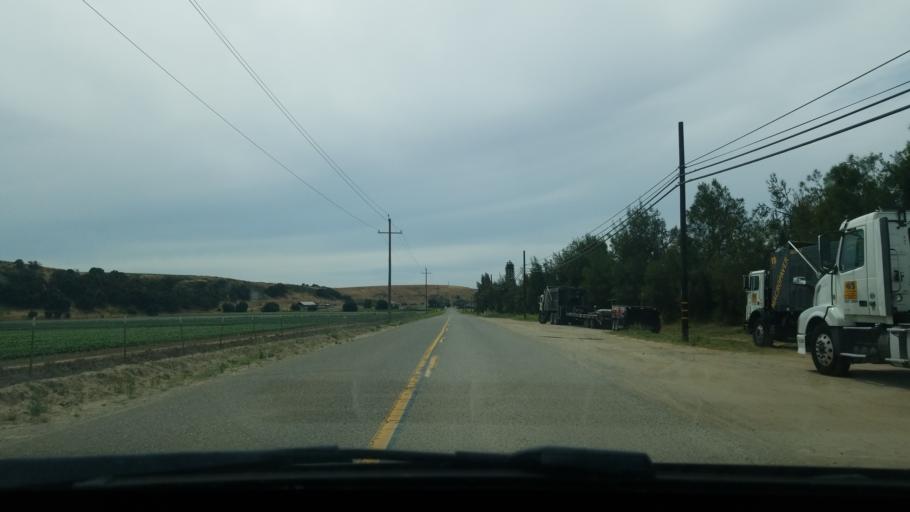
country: US
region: California
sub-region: Santa Barbara County
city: Los Alamos
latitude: 34.8645
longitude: -120.2822
